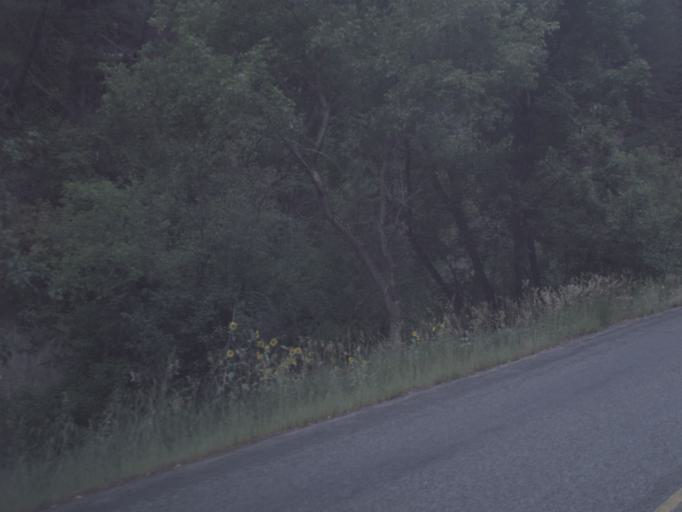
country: US
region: Utah
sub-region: Utah County
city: Orem
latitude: 40.3840
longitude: -111.5724
